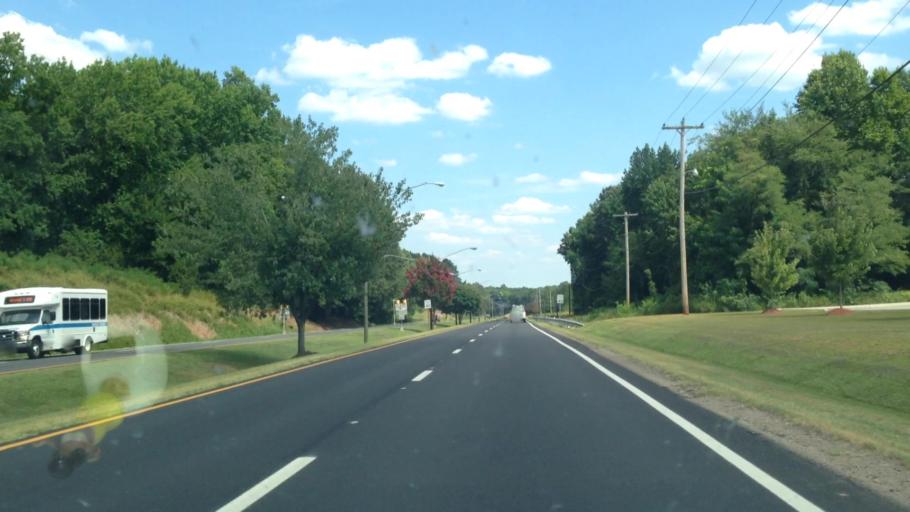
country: US
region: Virginia
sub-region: City of Danville
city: Danville
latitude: 36.5859
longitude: -79.4488
